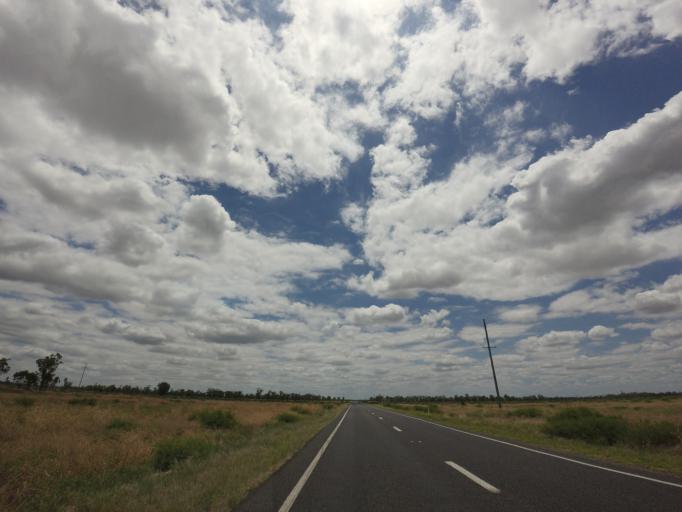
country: AU
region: New South Wales
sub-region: Moree Plains
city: Boggabilla
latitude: -28.6658
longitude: 150.3217
